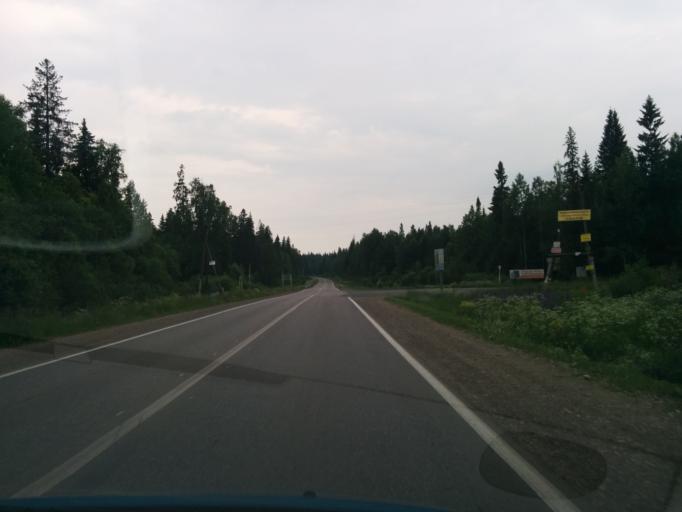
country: RU
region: Perm
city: Perm
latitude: 58.1964
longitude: 56.2097
